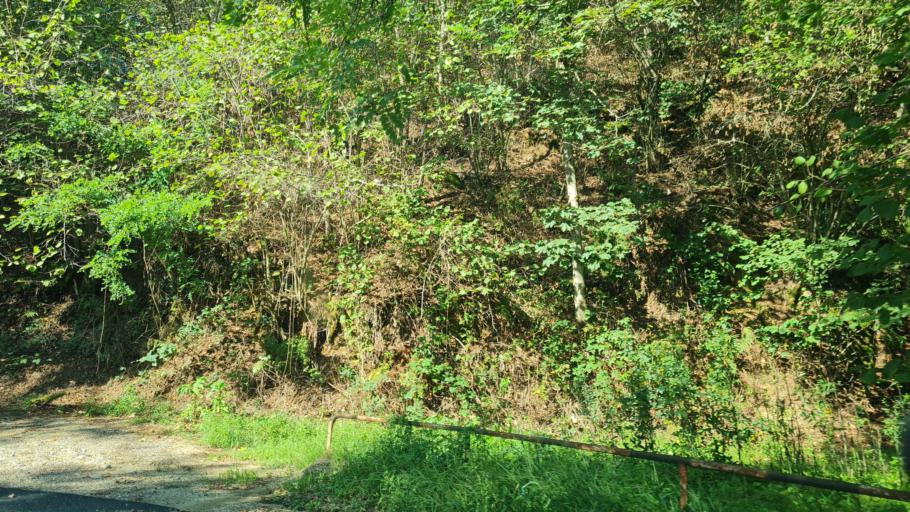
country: IT
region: Piedmont
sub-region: Provincia di Biella
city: Quaregna
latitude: 45.5886
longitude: 8.1637
